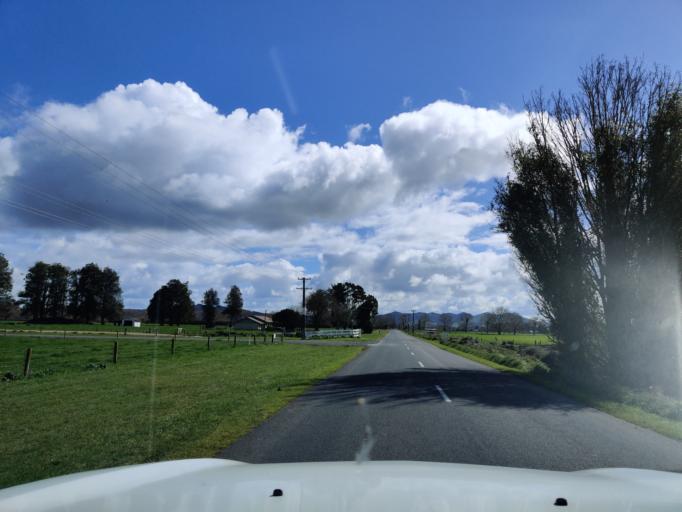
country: NZ
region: Waikato
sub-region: Waikato District
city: Ngaruawahia
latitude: -37.5813
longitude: 175.2772
